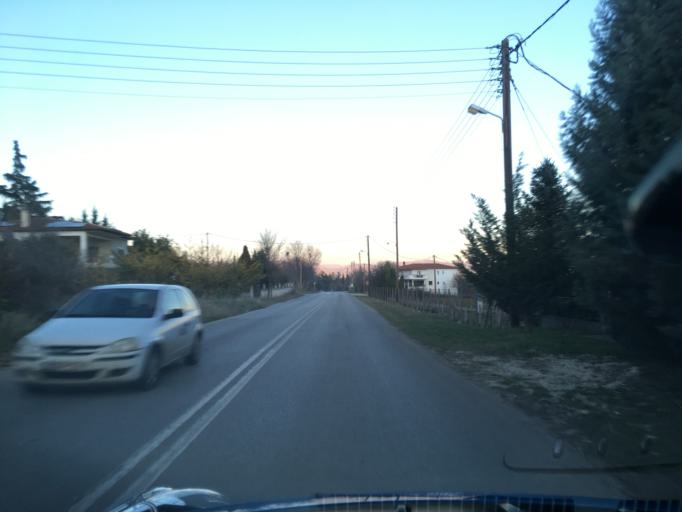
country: GR
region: West Macedonia
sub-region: Nomos Kozanis
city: Kozani
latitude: 40.2679
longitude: 21.7718
